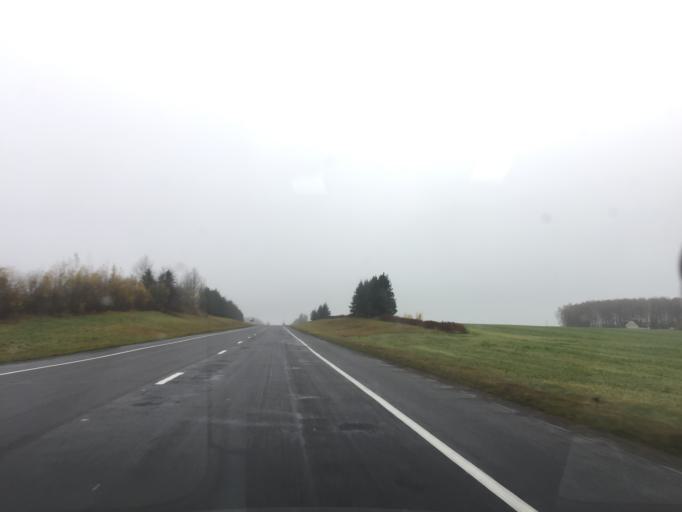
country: BY
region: Mogilev
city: Shklow
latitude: 54.2310
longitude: 30.4517
